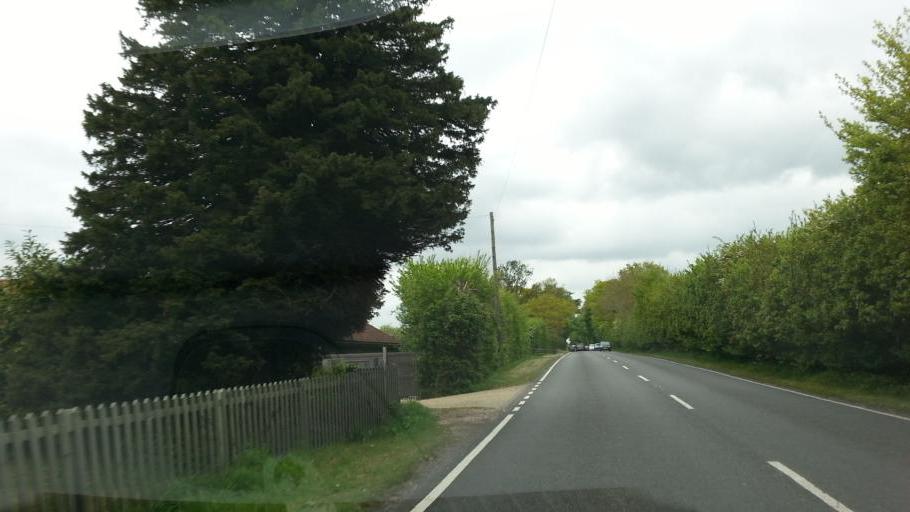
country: GB
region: England
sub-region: Suffolk
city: Lavenham
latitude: 52.1765
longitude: 0.7657
